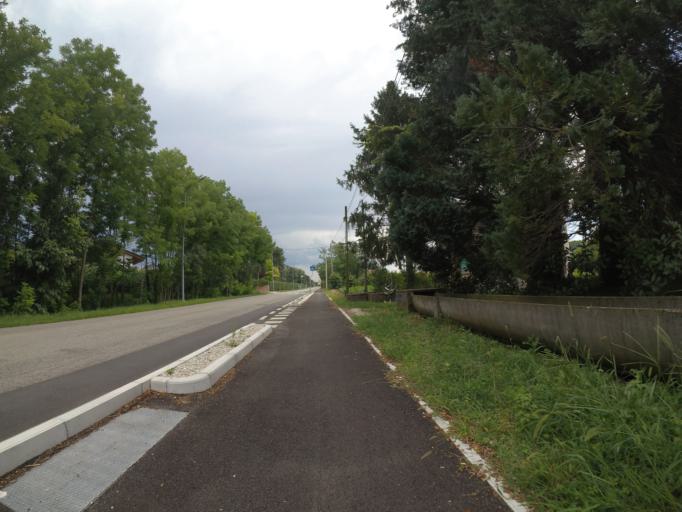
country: IT
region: Friuli Venezia Giulia
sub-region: Provincia di Udine
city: Talmassons
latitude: 45.9214
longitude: 13.1496
